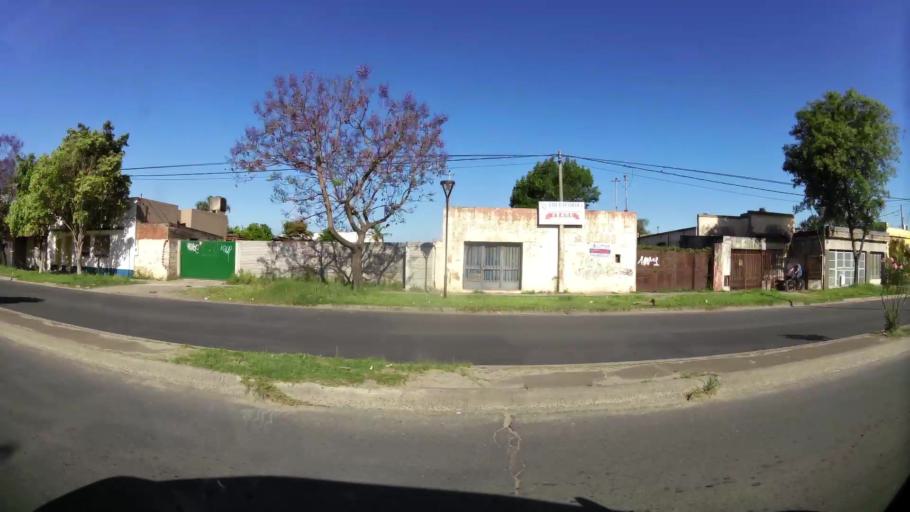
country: AR
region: Santa Fe
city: Santa Fe de la Vera Cruz
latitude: -31.6096
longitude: -60.7043
